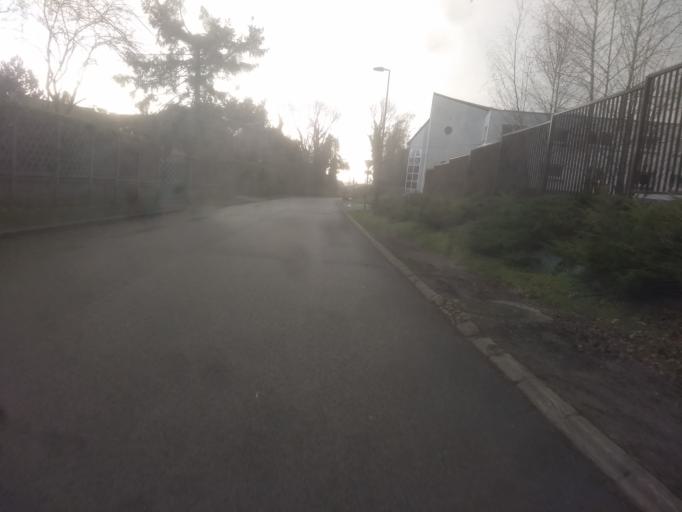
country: FR
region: Nord-Pas-de-Calais
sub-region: Departement du Pas-de-Calais
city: Saint-Laurent-Blangy
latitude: 50.3047
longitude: 2.8053
